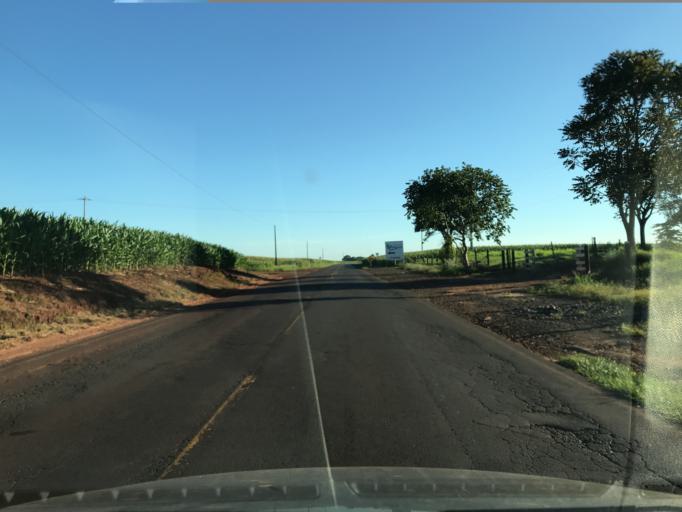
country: BR
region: Parana
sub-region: Palotina
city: Palotina
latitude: -24.1186
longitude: -53.8479
